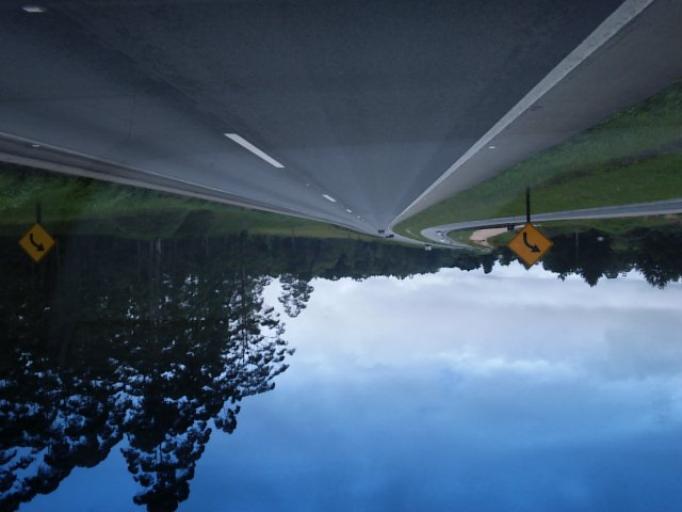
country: BR
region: Parana
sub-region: Piraquara
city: Piraquara
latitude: -25.4266
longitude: -49.0780
